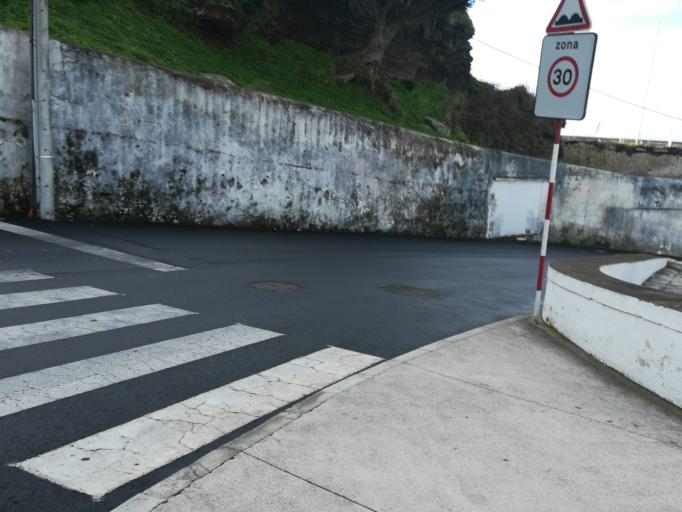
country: PT
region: Azores
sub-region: Angra do Heroismo
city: Angra do Heroismo
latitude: 38.6522
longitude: -27.2129
